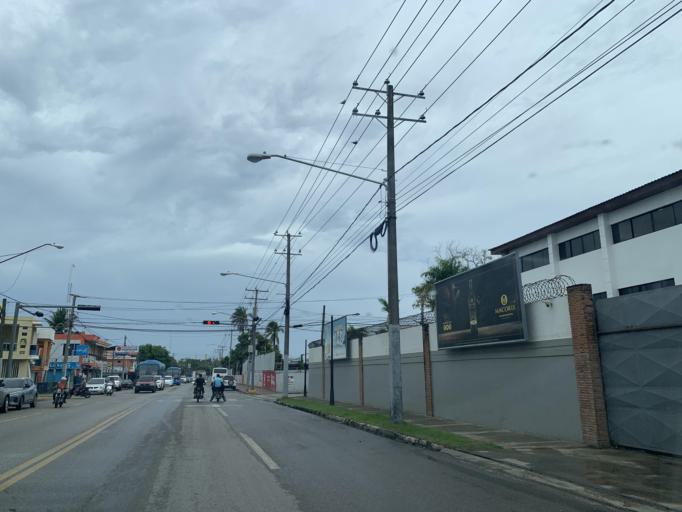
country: DO
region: Puerto Plata
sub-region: Puerto Plata
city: Puerto Plata
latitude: 19.7955
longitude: -70.6985
